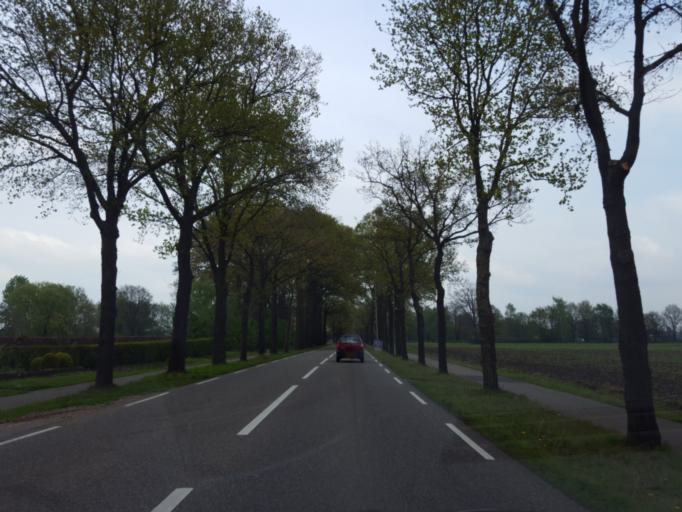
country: NL
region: Limburg
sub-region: Gemeente Weert
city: Weert
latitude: 51.2584
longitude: 5.6486
